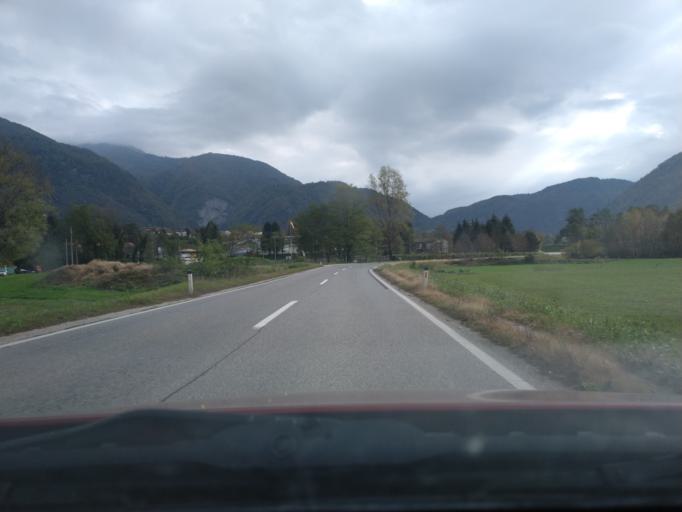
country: SI
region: Tolmin
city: Tolmin
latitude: 46.1826
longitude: 13.7227
